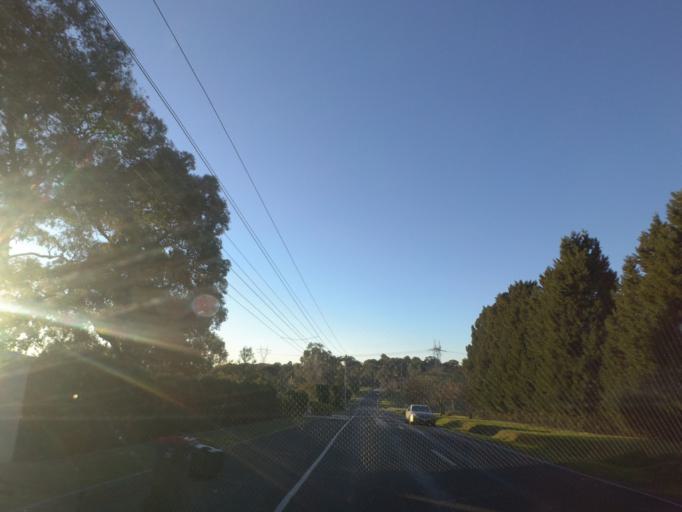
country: AU
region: Victoria
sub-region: Manningham
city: Park Orchards
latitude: -37.7633
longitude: 145.1969
